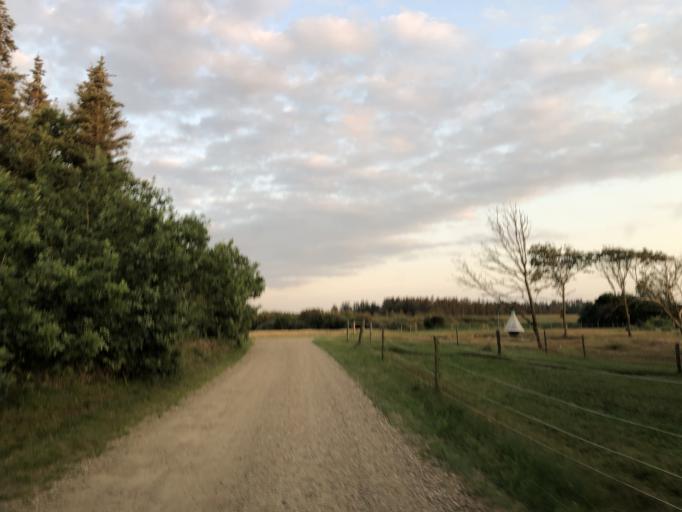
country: DK
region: Central Jutland
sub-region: Holstebro Kommune
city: Vinderup
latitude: 56.4608
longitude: 8.8967
